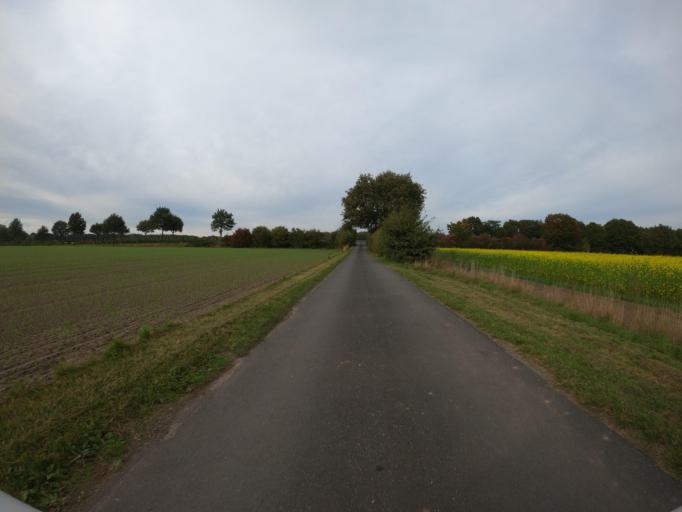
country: DE
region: North Rhine-Westphalia
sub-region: Regierungsbezirk Dusseldorf
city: Schermbeck
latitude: 51.6969
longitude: 6.8985
